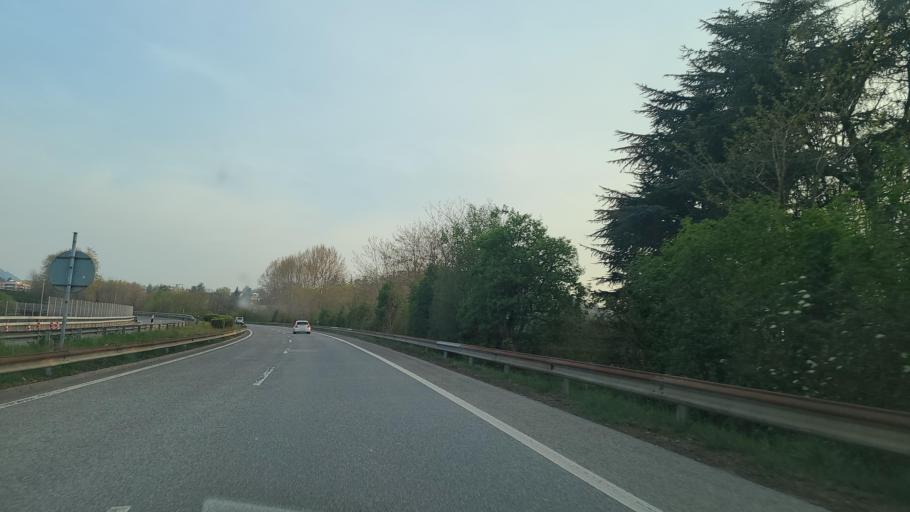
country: CH
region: Ticino
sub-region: Lugano District
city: Massagno
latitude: 46.0197
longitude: 8.9322
